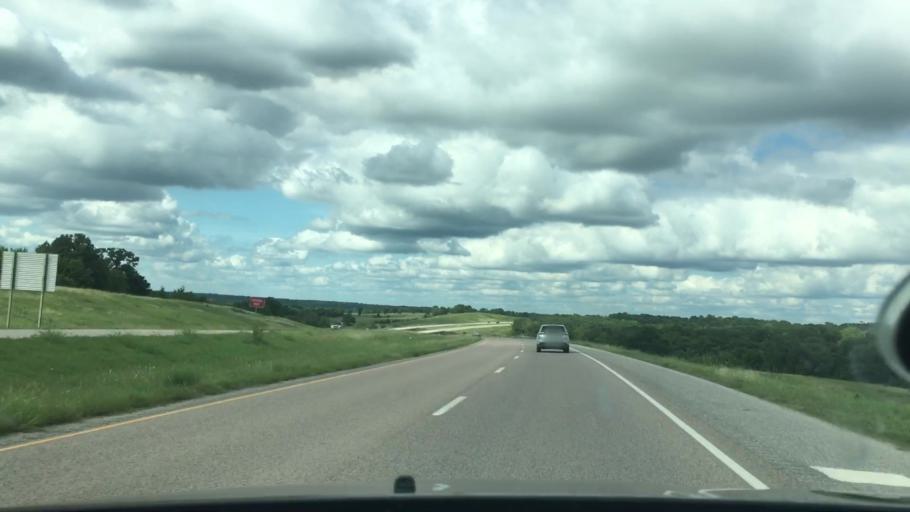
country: US
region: Oklahoma
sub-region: Pontotoc County
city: Ada
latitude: 34.8039
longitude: -96.6948
